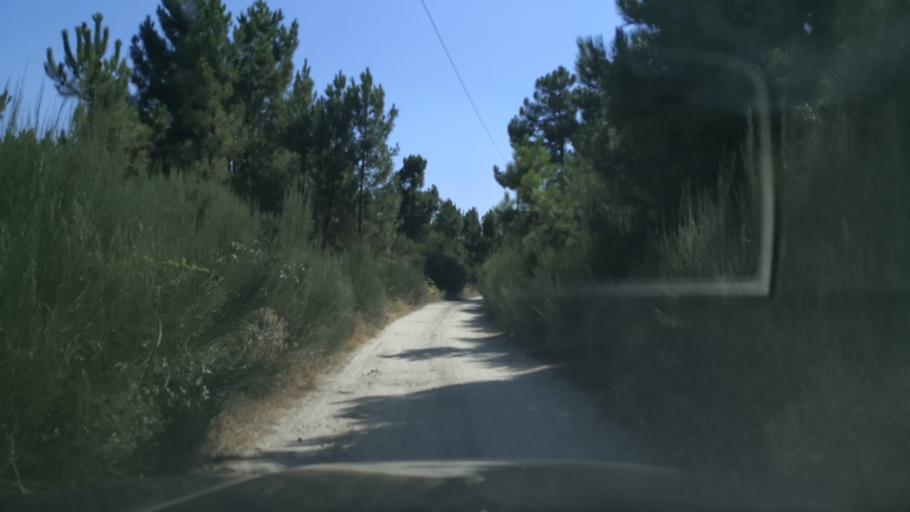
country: PT
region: Vila Real
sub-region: Murca
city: Murca
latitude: 41.3437
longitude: -7.4744
